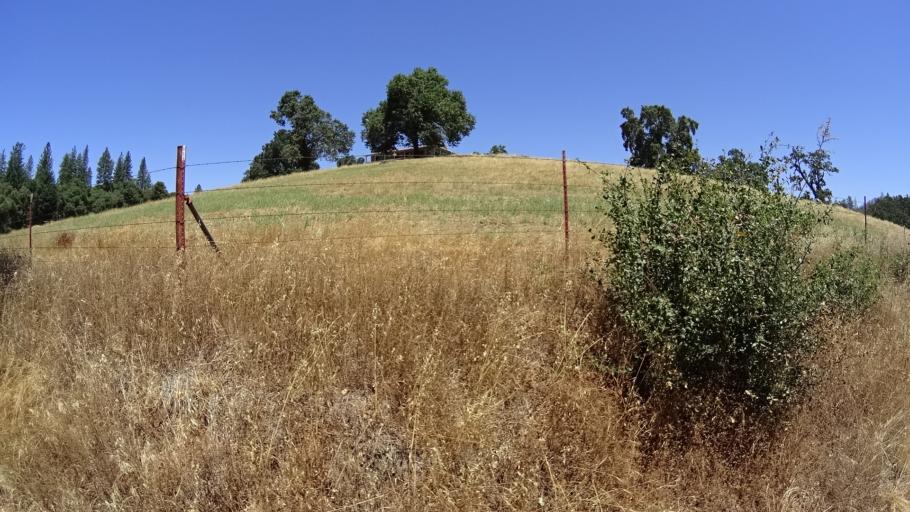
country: US
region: California
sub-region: Calaveras County
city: Mountain Ranch
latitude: 38.2364
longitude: -120.5590
